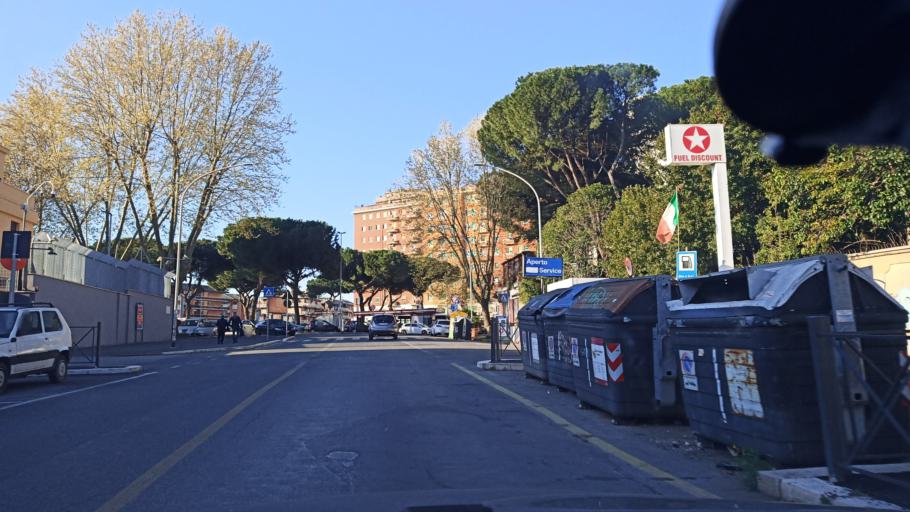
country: IT
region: Latium
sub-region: Citta metropolitana di Roma Capitale
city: Rome
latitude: 41.8772
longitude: 12.5104
